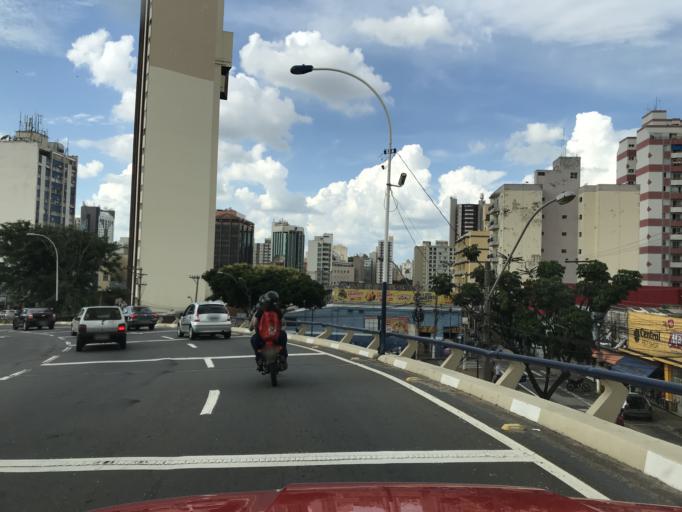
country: BR
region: Sao Paulo
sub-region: Campinas
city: Campinas
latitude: -22.9095
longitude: -47.0616
